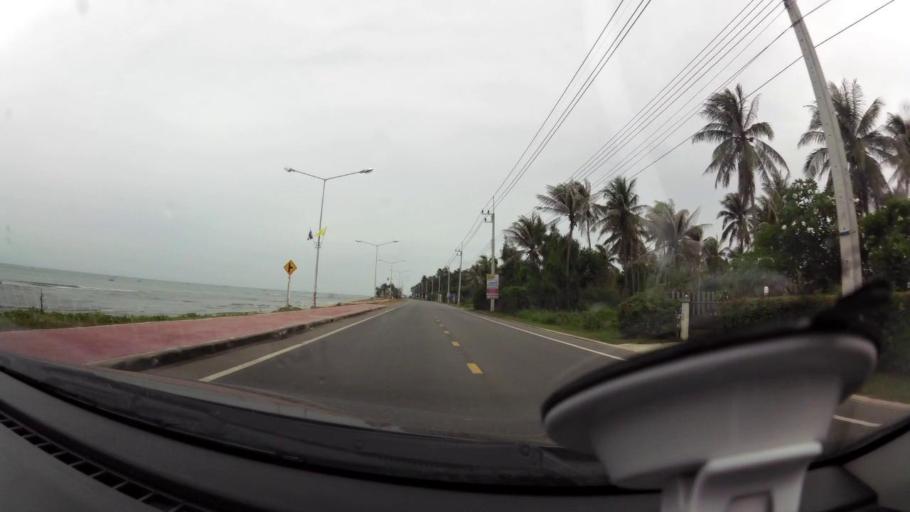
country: TH
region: Prachuap Khiri Khan
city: Pran Buri
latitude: 12.3912
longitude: 99.9971
